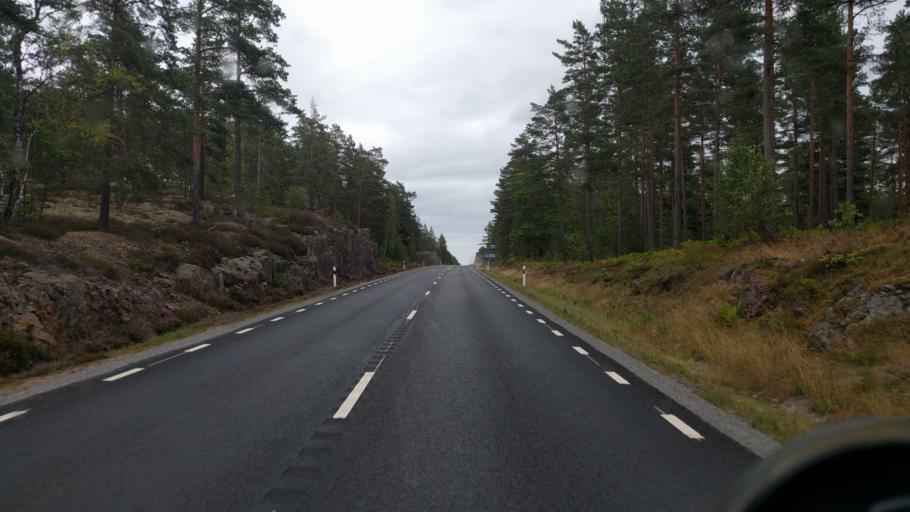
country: SE
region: Kalmar
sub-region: Vasterviks Kommun
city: Ankarsrum
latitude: 57.7236
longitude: 16.4137
